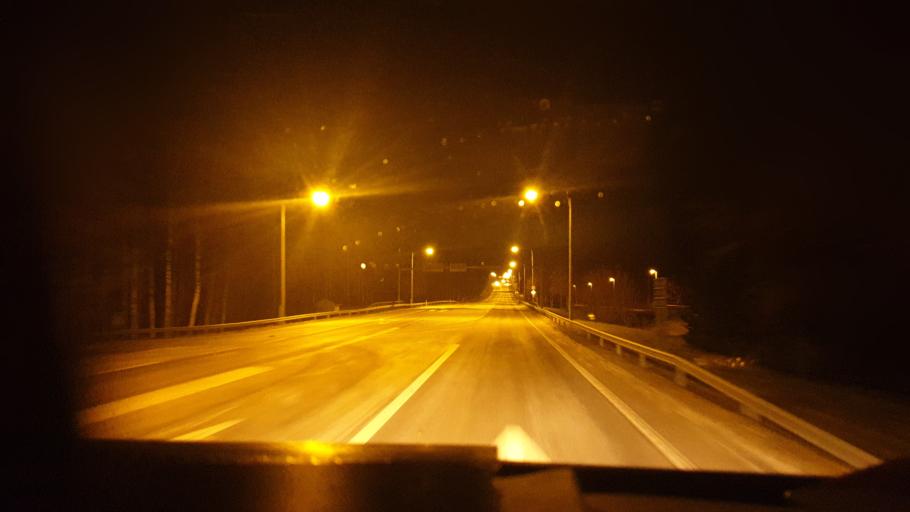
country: FI
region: Southern Ostrobothnia
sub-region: Kuusiokunnat
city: Alavus
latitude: 62.5946
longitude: 23.6249
